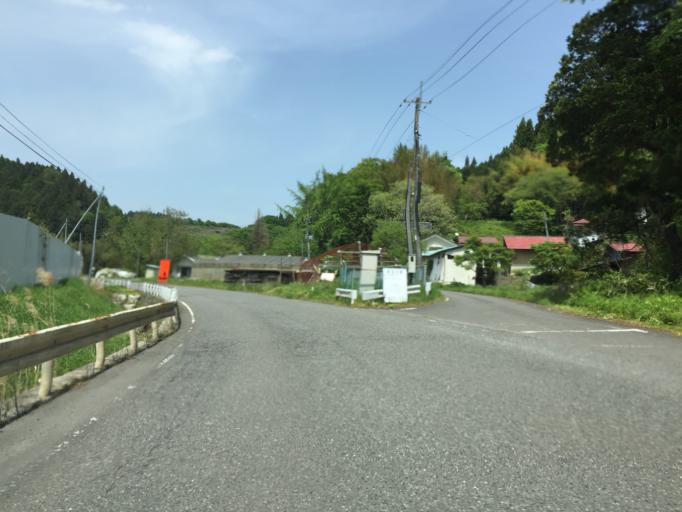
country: JP
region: Fukushima
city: Ishikawa
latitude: 37.1842
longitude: 140.4777
